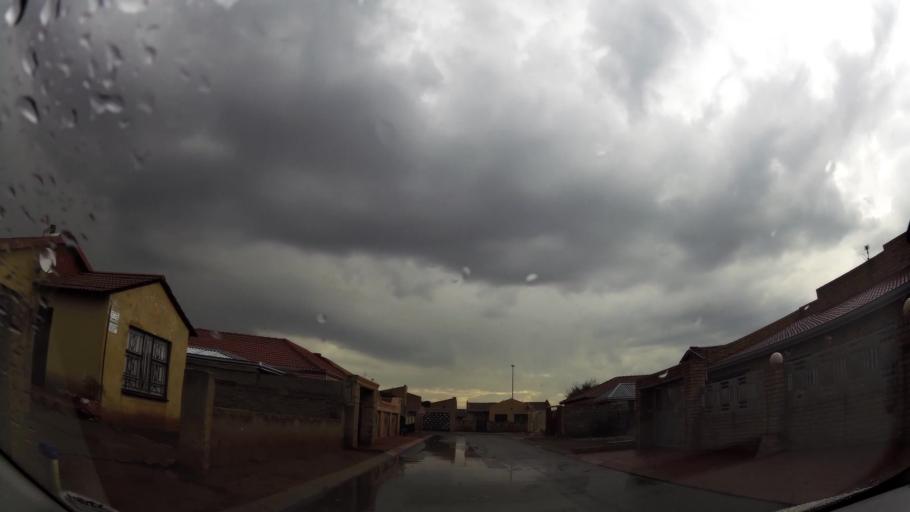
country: ZA
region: Gauteng
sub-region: Ekurhuleni Metropolitan Municipality
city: Germiston
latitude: -26.3628
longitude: 28.1350
